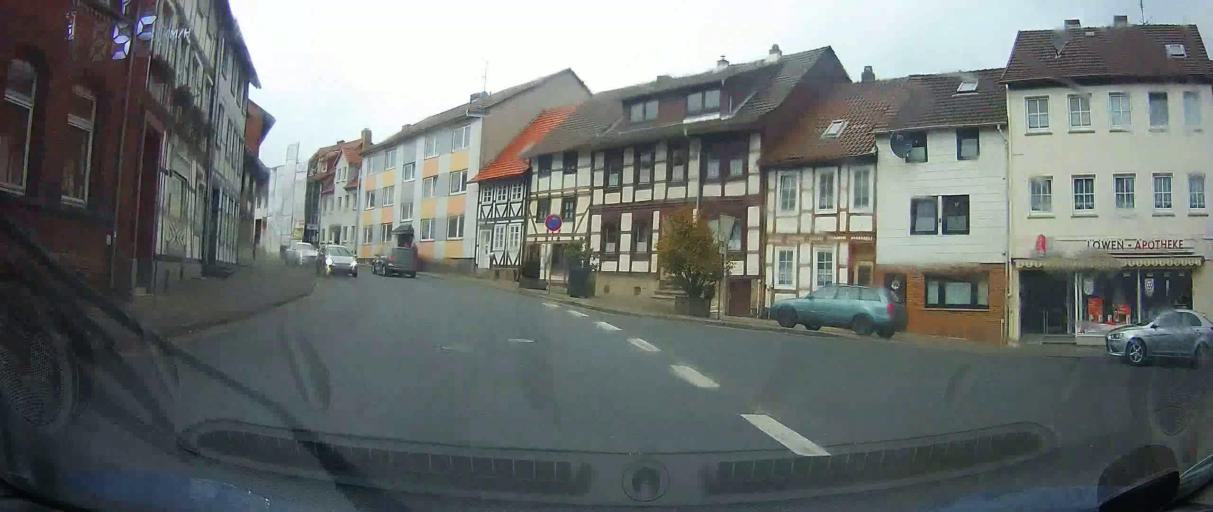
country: DE
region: Lower Saxony
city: Uslar
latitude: 51.6602
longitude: 9.6393
